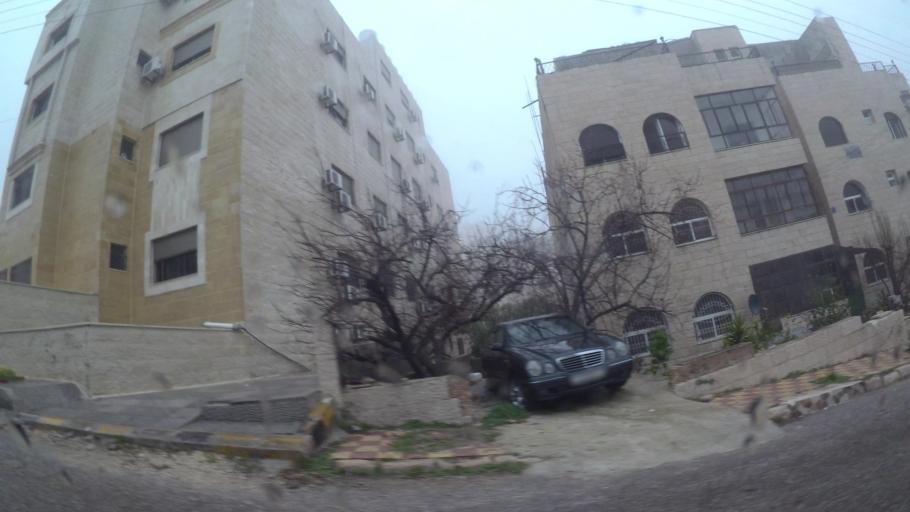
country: JO
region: Amman
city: Al Jubayhah
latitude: 32.0085
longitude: 35.8793
